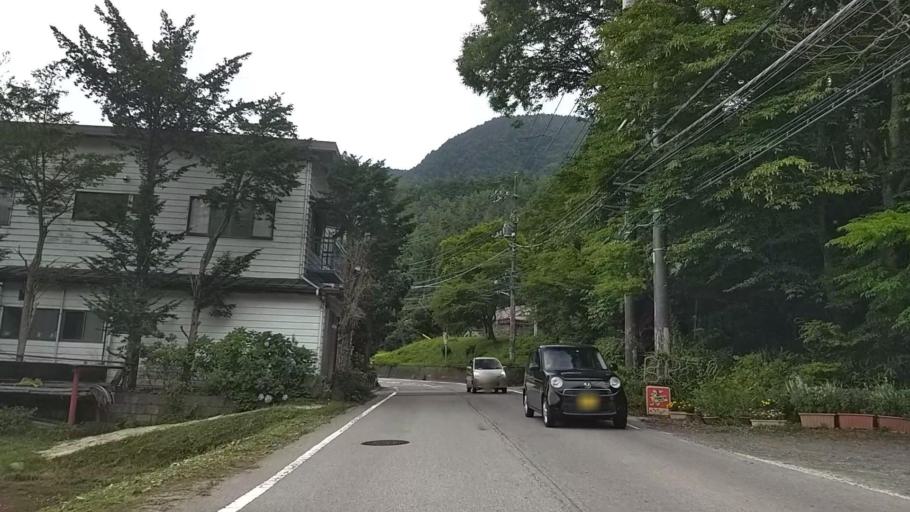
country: JP
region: Yamanashi
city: Fujikawaguchiko
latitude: 35.5049
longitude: 138.7153
